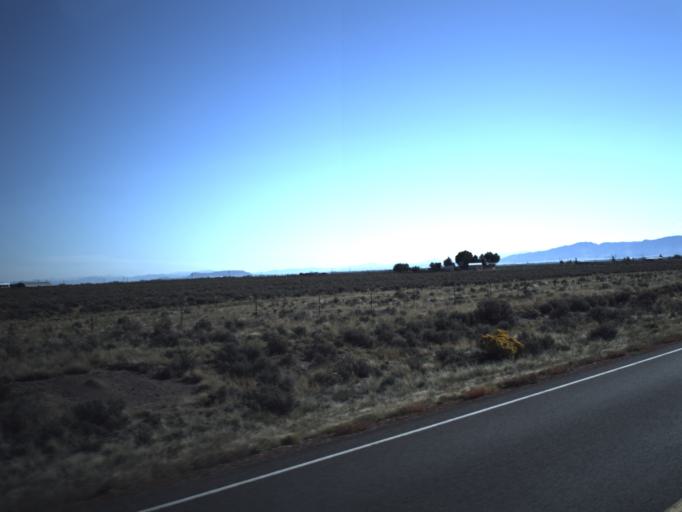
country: US
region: Utah
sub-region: Washington County
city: Enterprise
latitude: 37.7598
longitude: -113.7981
